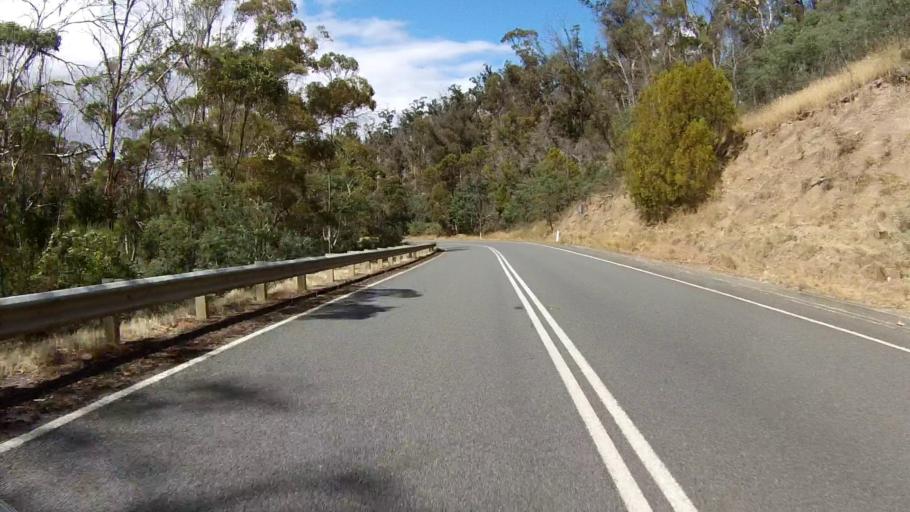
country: AU
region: Tasmania
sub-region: Sorell
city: Sorell
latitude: -42.6086
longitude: 147.6563
